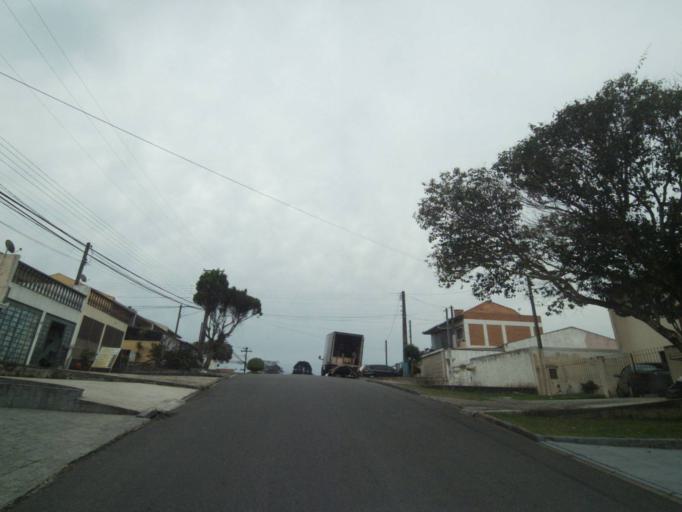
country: BR
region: Parana
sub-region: Pinhais
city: Pinhais
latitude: -25.3991
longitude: -49.2061
